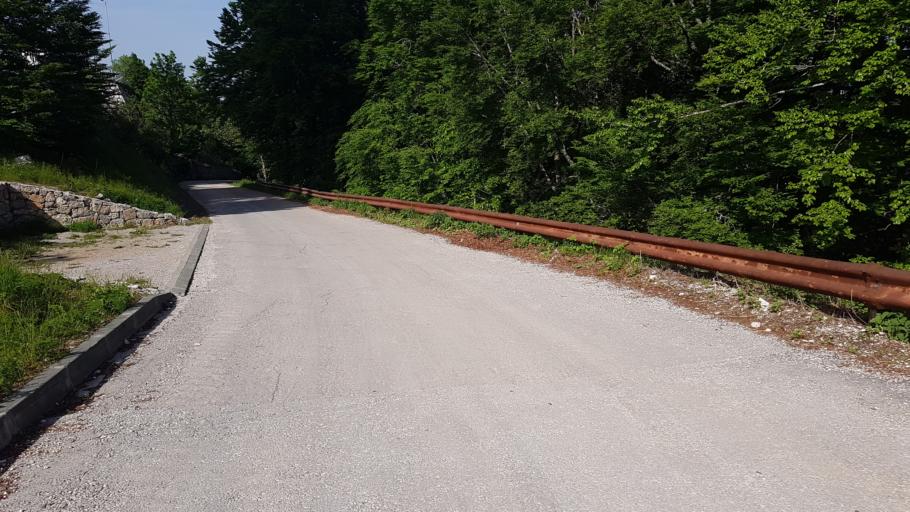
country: HR
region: Istarska
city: Lovran
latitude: 45.2863
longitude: 14.2026
